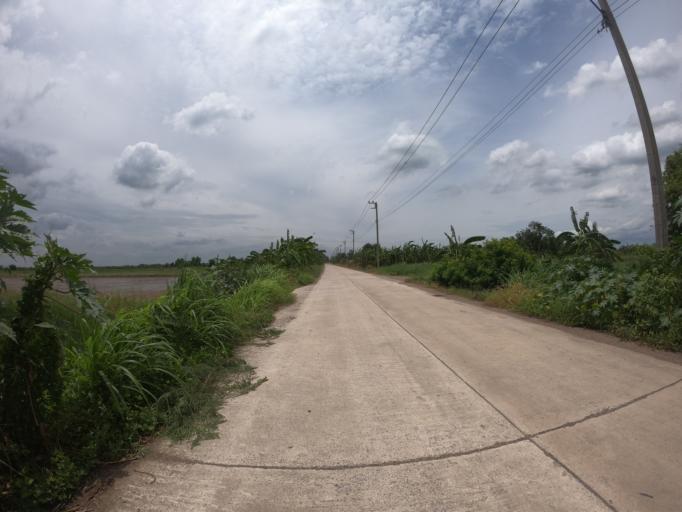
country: TH
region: Pathum Thani
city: Ban Lam Luk Ka
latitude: 14.0194
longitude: 100.8653
